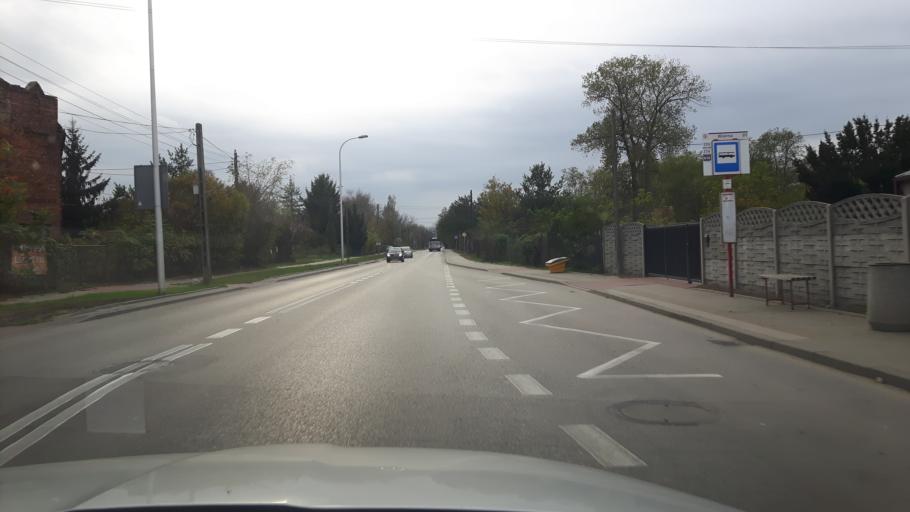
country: PL
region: Masovian Voivodeship
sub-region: Powiat wolominski
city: Zabki
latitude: 52.2729
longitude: 21.0851
